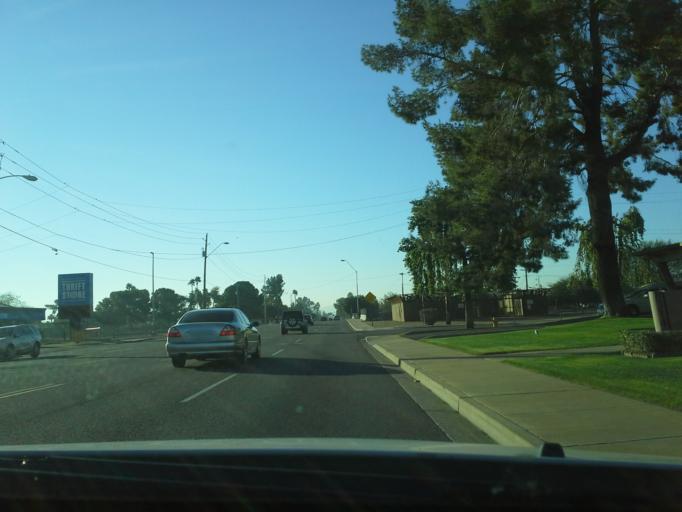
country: US
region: Arizona
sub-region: Maricopa County
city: Phoenix
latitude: 33.5590
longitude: -112.0654
